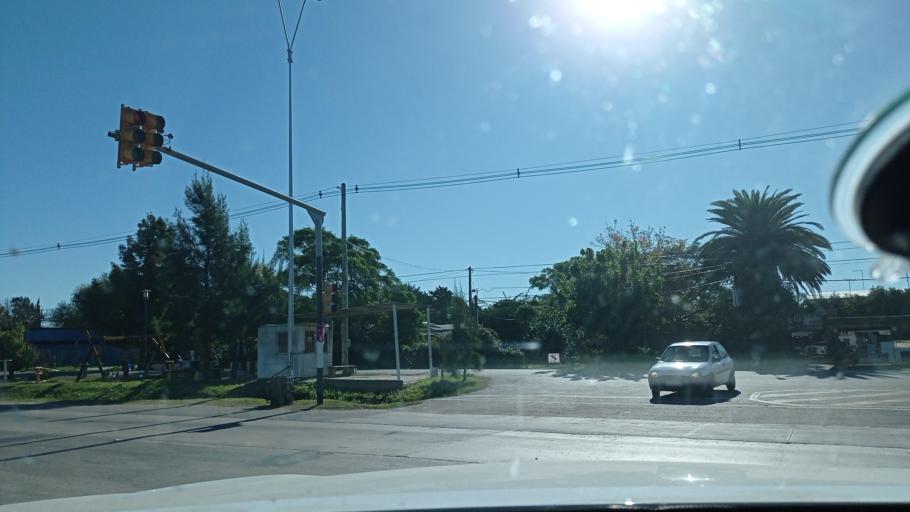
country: UY
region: Canelones
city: Joaquin Suarez
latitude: -34.7520
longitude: -56.0006
